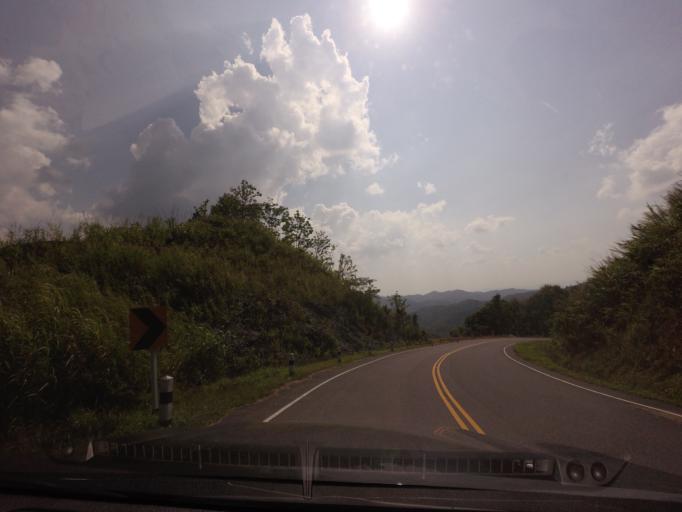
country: TH
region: Nan
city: Santi Suk
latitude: 18.9738
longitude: 101.0382
